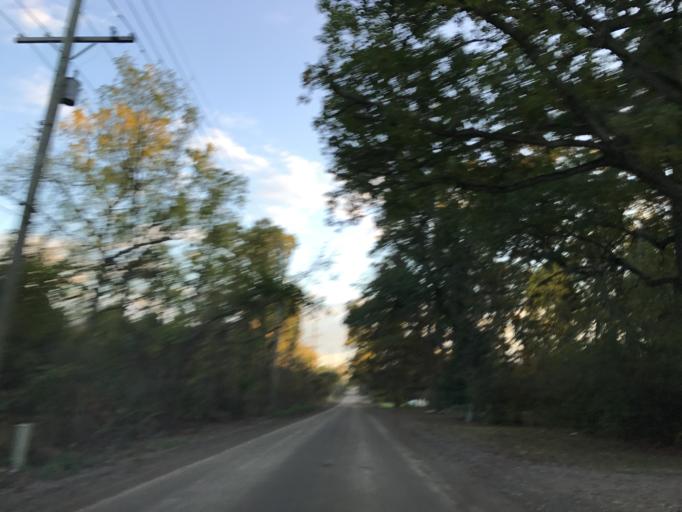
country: US
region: Michigan
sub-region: Oakland County
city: South Lyon
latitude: 42.4972
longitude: -83.6390
